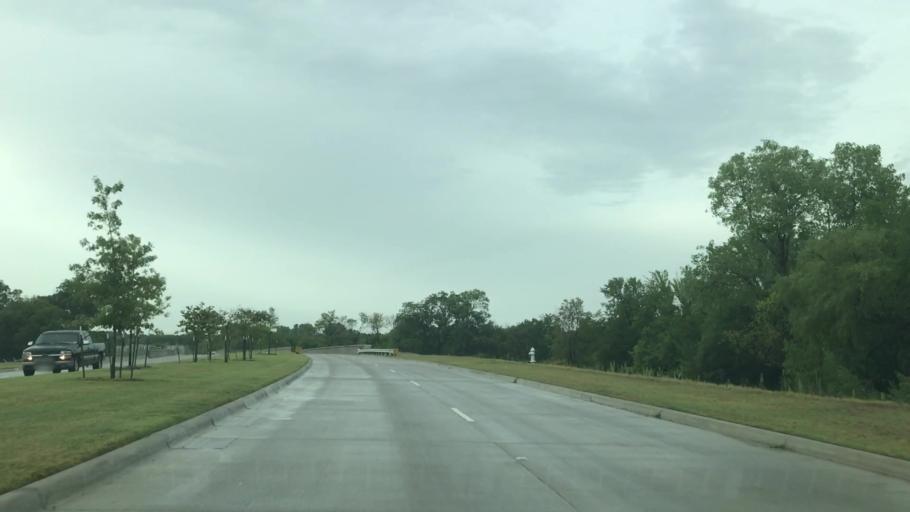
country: US
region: Texas
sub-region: Denton County
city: Lewisville
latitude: 33.0532
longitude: -96.9811
